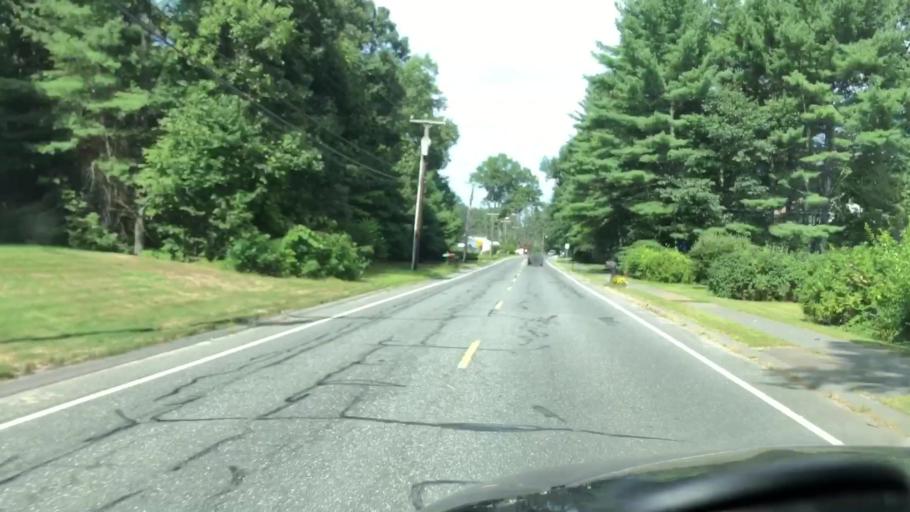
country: US
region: Massachusetts
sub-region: Hampshire County
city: Southampton
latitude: 42.2488
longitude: -72.7231
